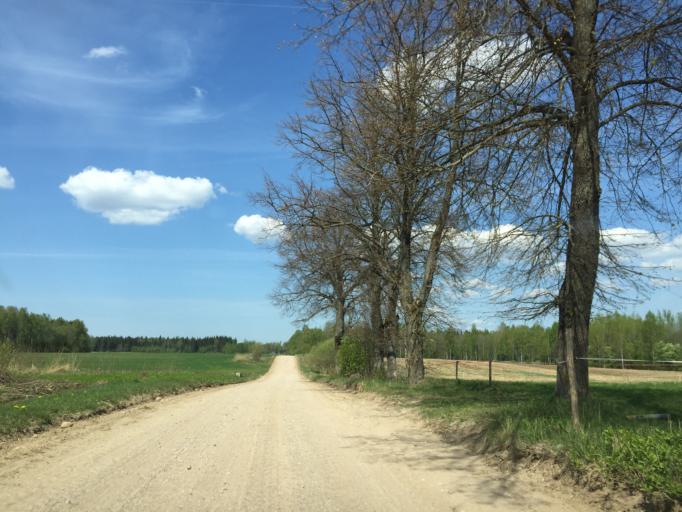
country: LV
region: Limbazu Rajons
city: Limbazi
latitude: 57.3568
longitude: 24.6438
